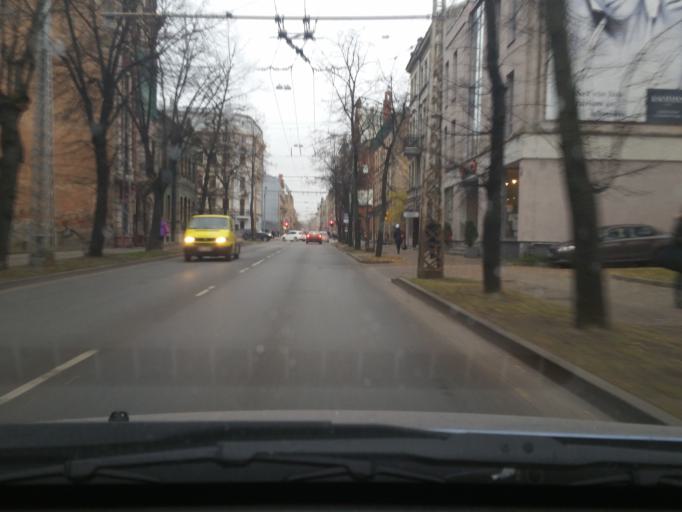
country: LV
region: Riga
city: Riga
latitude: 56.9641
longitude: 24.1355
